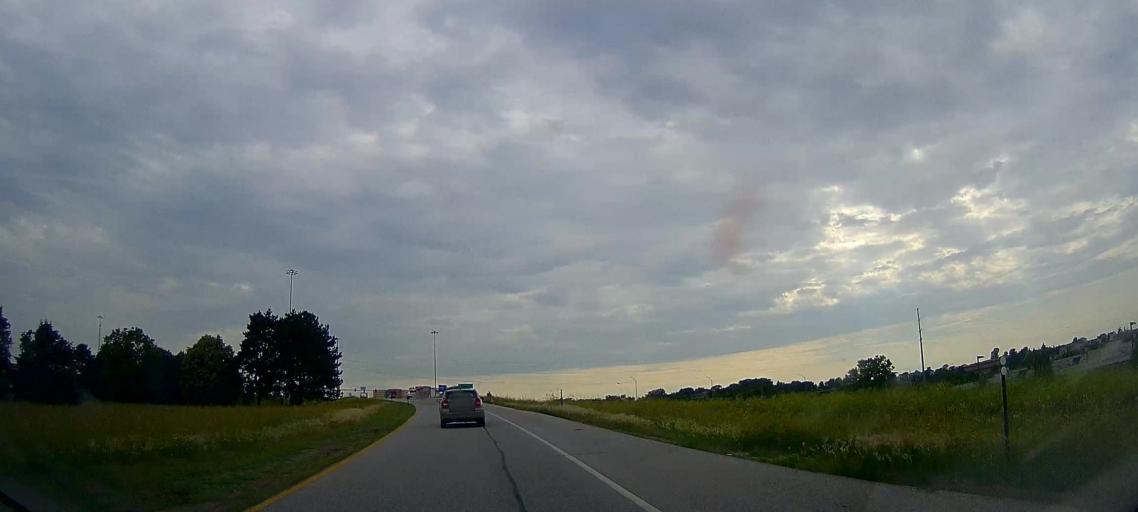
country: US
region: Nebraska
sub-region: Douglas County
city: Bennington
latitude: 41.3244
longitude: -96.0681
